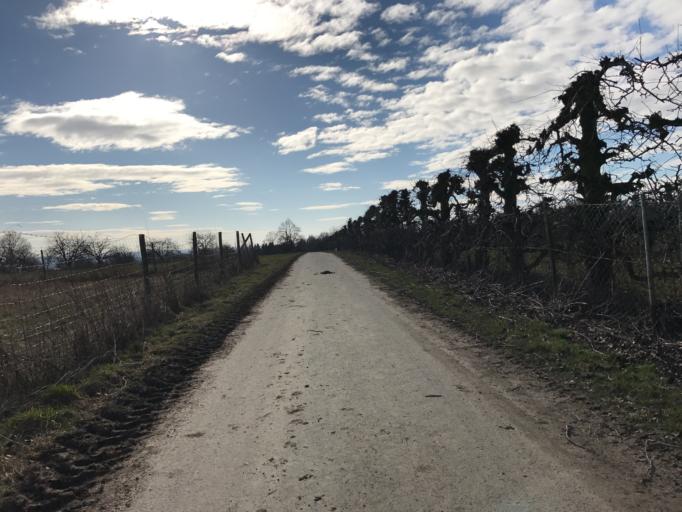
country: DE
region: Hesse
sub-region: Regierungsbezirk Darmstadt
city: Niedernhausen
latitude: 50.1002
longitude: 8.3133
